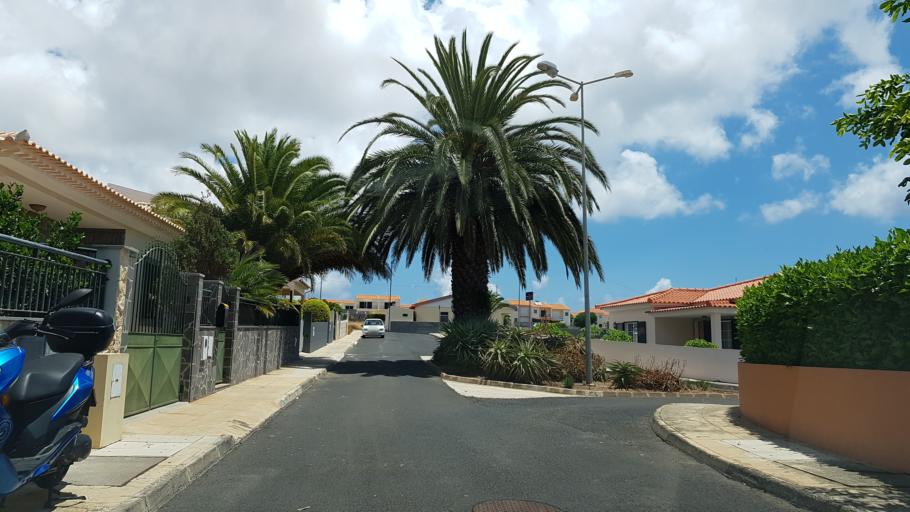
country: PT
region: Madeira
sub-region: Porto Santo
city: Vila de Porto Santo
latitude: 33.0618
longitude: -16.3564
